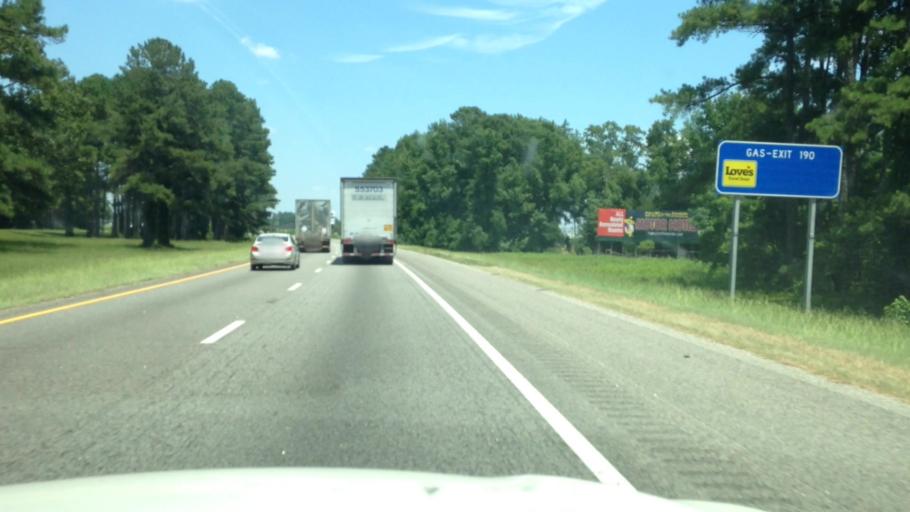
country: US
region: South Carolina
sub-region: Dillon County
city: Dillon
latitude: 34.4116
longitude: -79.4211
